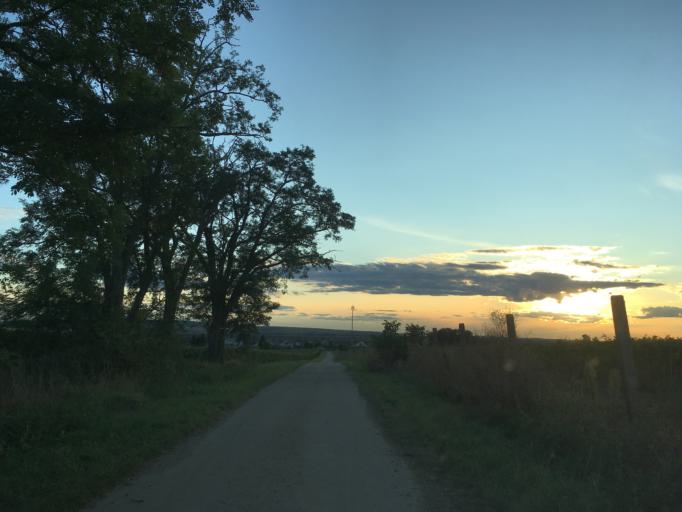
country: SK
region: Nitriansky
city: Svodin
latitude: 47.9048
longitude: 18.4305
